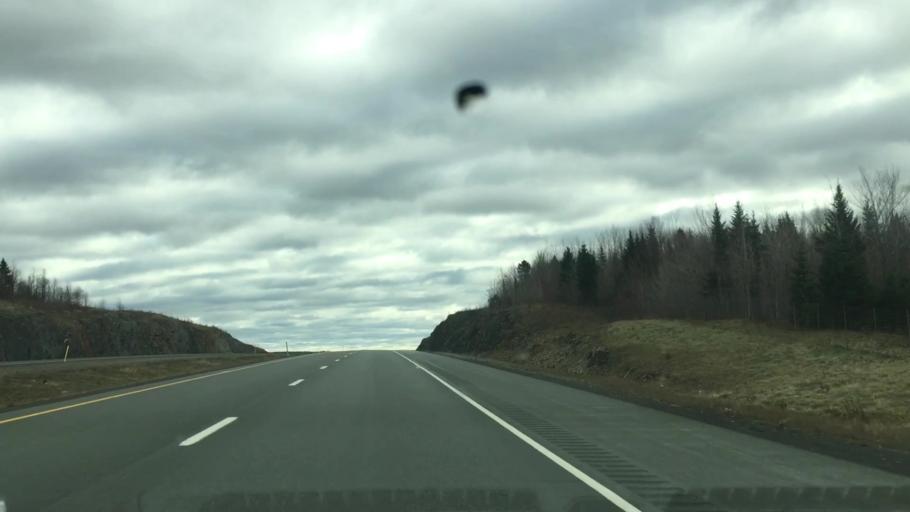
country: CA
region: New Brunswick
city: Florenceville-Bristol
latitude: 46.5509
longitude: -67.7344
